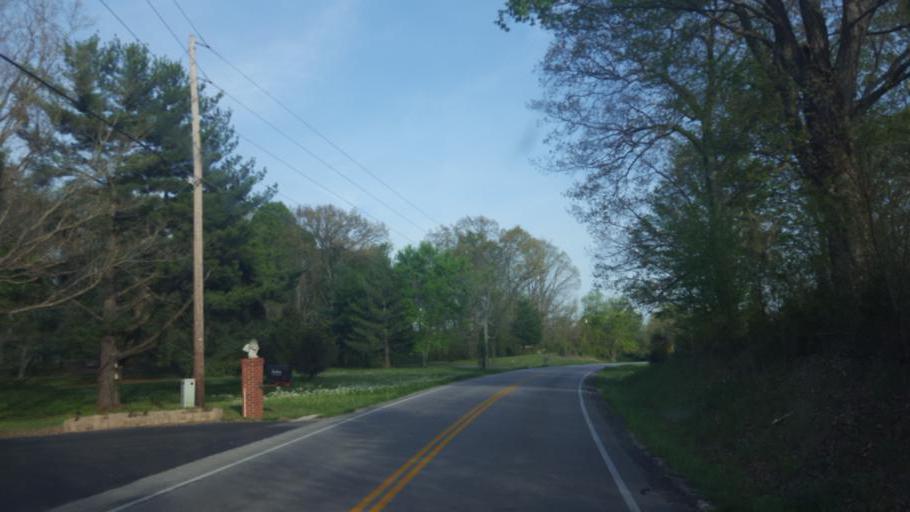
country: US
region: Kentucky
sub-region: Warren County
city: Bowling Green
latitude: 36.9612
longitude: -86.3576
